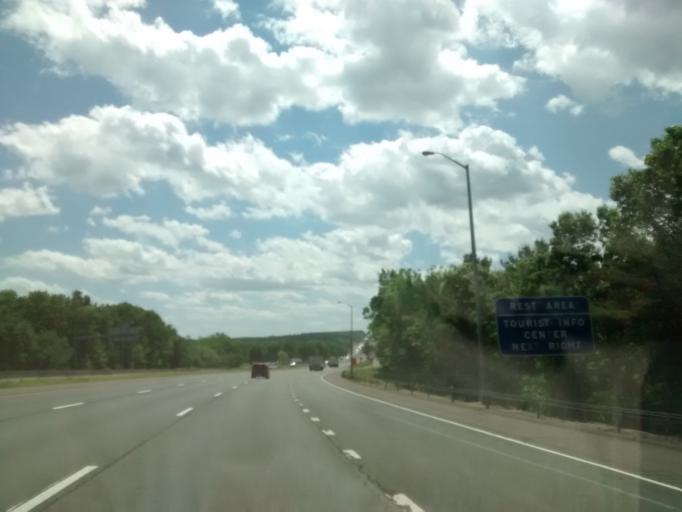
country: US
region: Connecticut
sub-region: Tolland County
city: Stafford Springs
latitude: 41.8960
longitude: -72.2915
